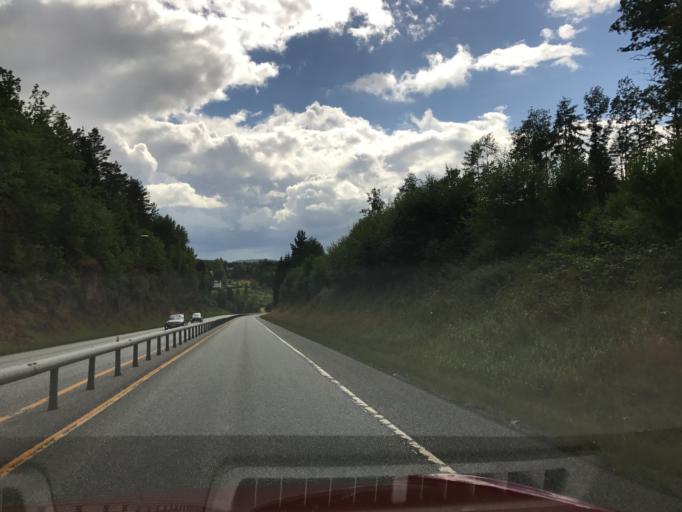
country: NO
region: Aust-Agder
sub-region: Gjerstad
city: Gjerstad
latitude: 58.8479
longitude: 9.1142
